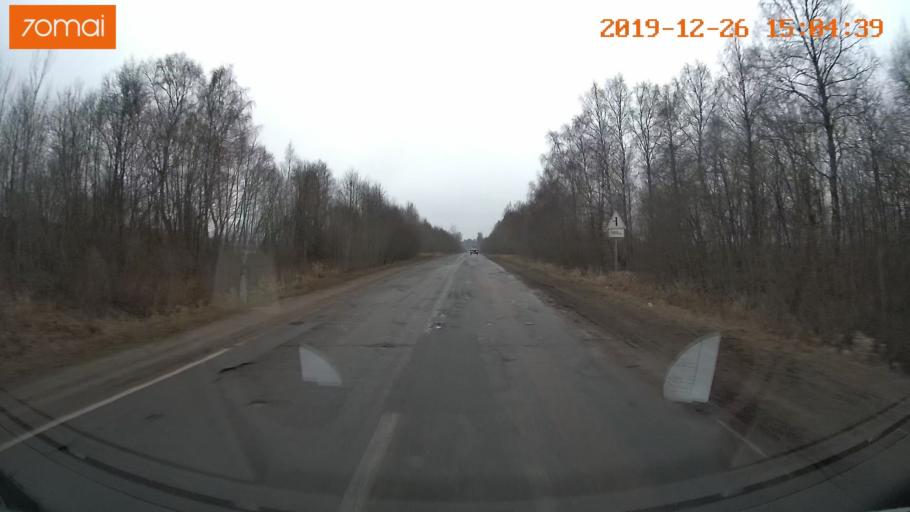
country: RU
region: Jaroslavl
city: Rybinsk
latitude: 58.1975
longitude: 38.8596
